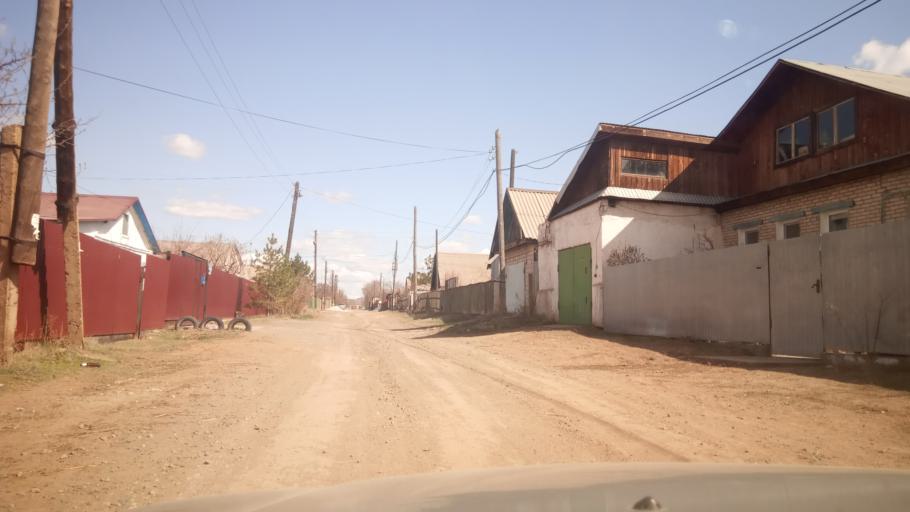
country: RU
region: Orenburg
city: Novotroitsk
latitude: 51.2055
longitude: 58.3152
